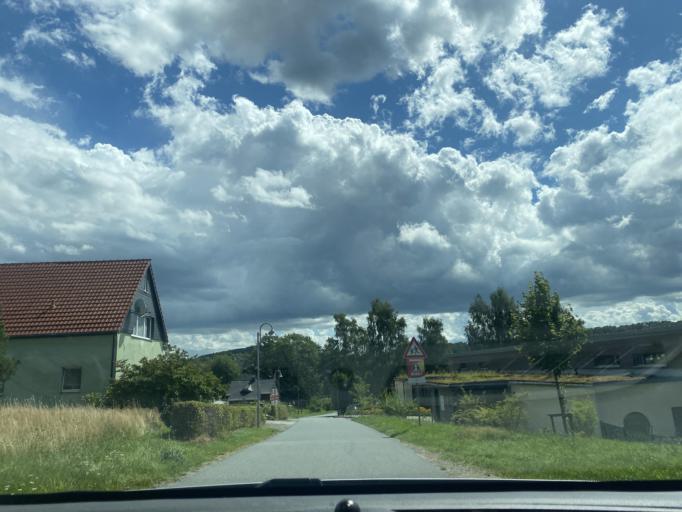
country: DE
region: Saxony
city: Beiersdorf
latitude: 51.0730
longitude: 14.5339
